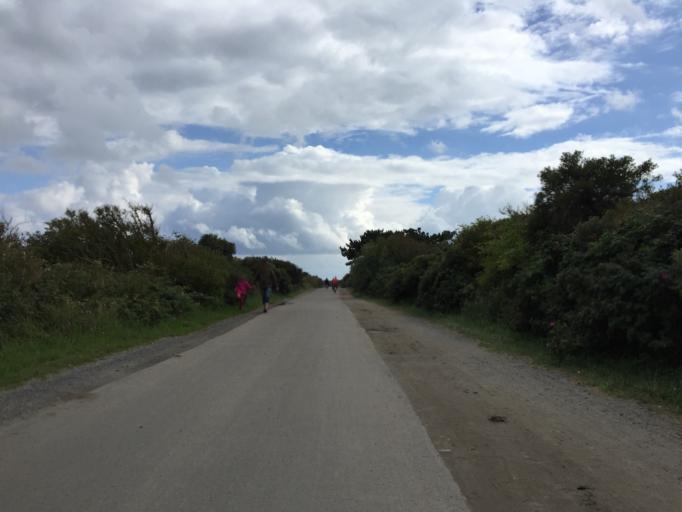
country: DE
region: Mecklenburg-Vorpommern
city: Hiddensee
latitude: 54.5831
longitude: 13.1023
